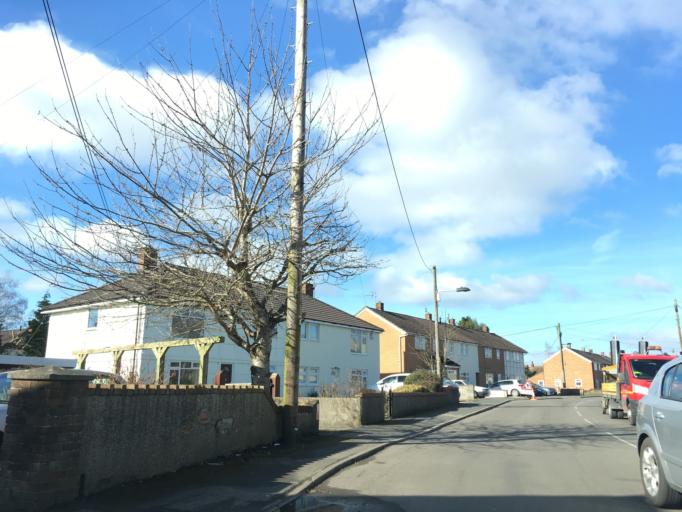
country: GB
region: England
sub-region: South Gloucestershire
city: Winterbourne
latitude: 51.5290
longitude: -2.4954
